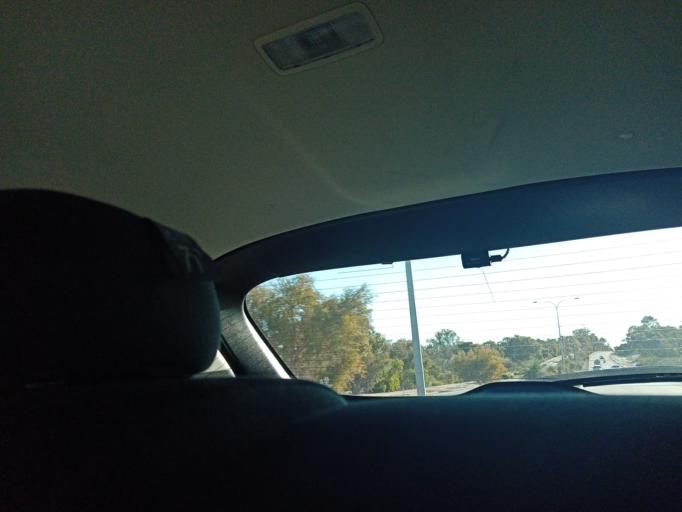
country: AU
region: Western Australia
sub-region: City of Cockburn
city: South Lake
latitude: -32.1255
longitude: 115.8320
